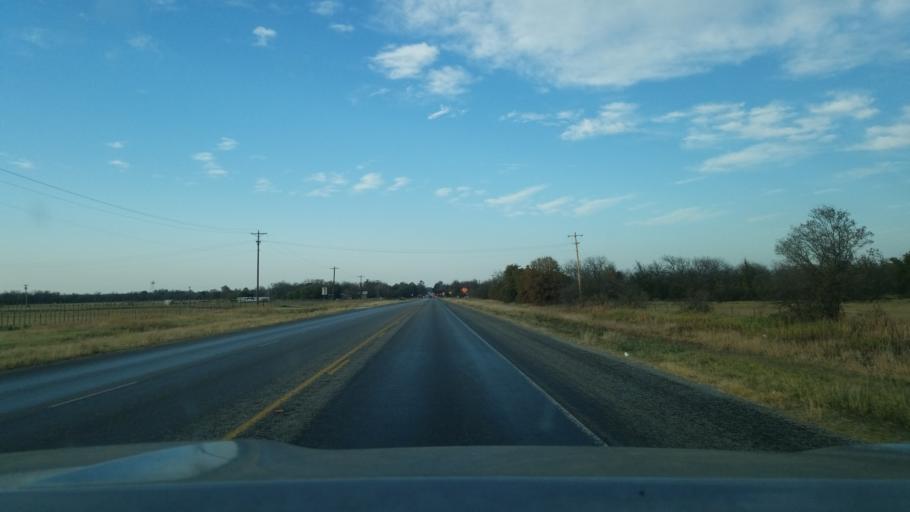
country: US
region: Texas
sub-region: Brown County
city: Lake Brownwood
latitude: 32.0807
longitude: -98.9640
